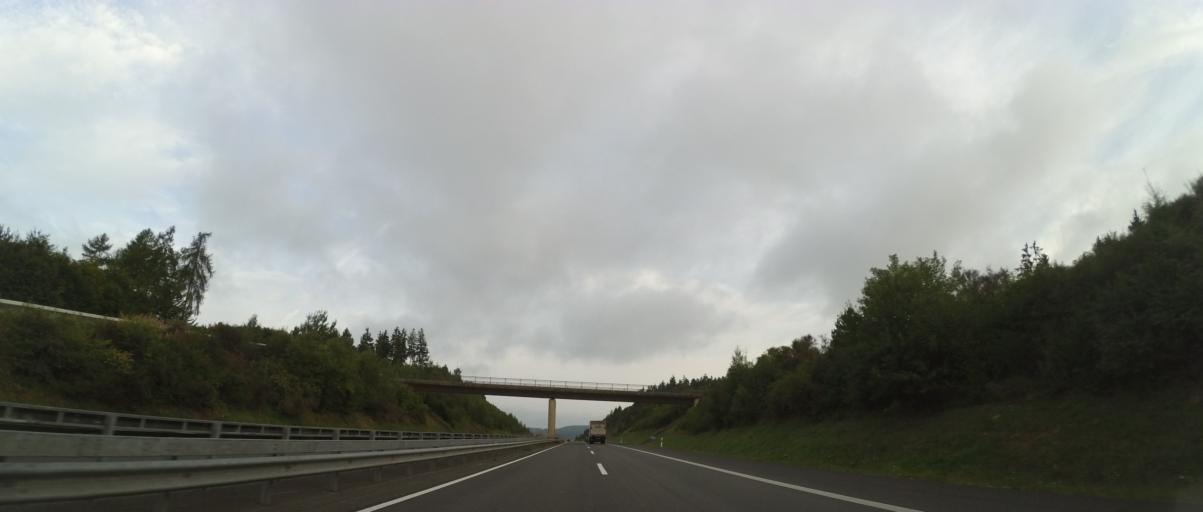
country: DE
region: Rheinland-Pfalz
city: Horscheid
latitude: 50.2193
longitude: 6.8620
